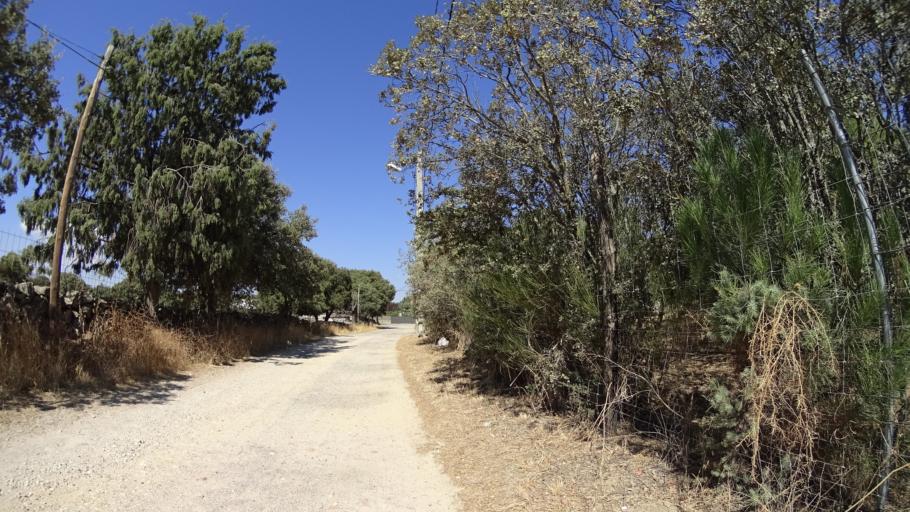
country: ES
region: Madrid
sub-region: Provincia de Madrid
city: Collado-Villalba
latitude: 40.6144
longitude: -4.0043
